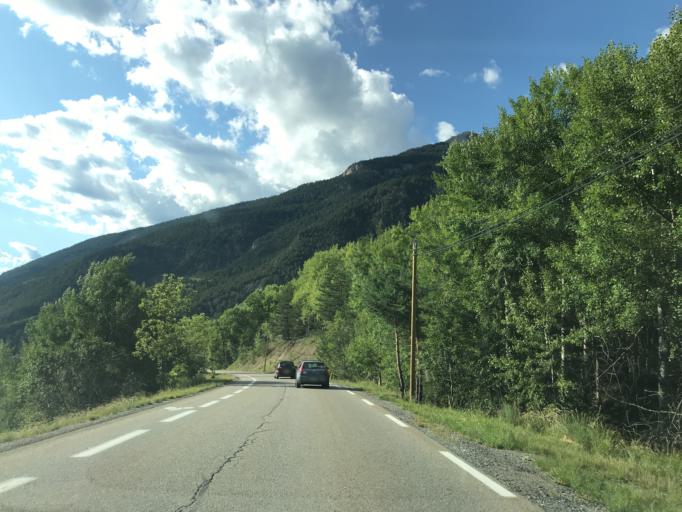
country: FR
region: Provence-Alpes-Cote d'Azur
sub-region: Departement des Hautes-Alpes
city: Briancon
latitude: 44.8737
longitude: 6.6935
